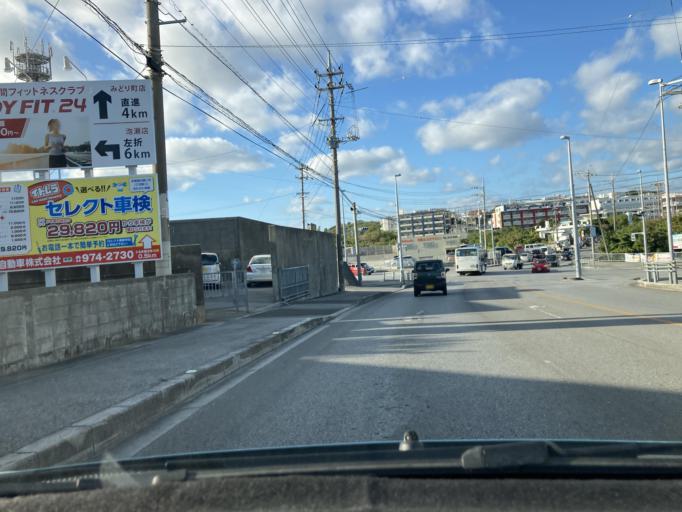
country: JP
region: Okinawa
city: Katsuren-haebaru
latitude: 26.3458
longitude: 127.8711
